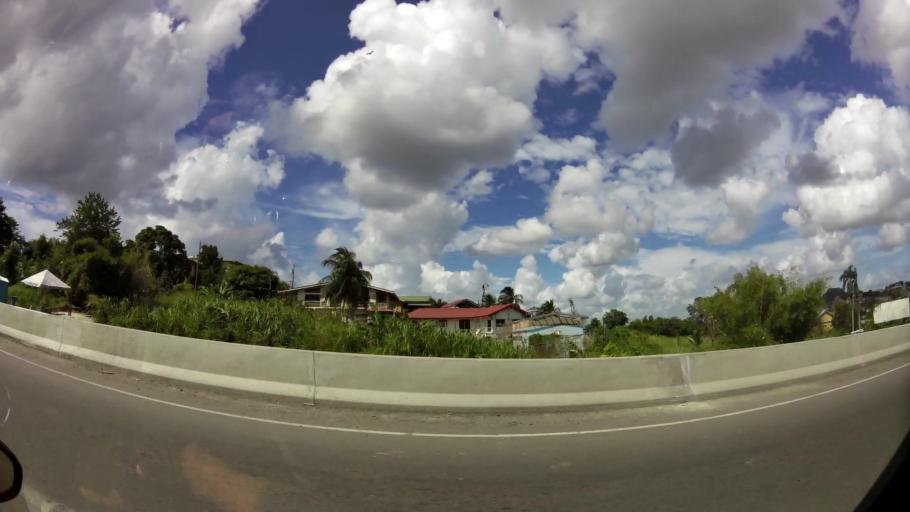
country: TT
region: City of San Fernando
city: San Fernando
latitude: 10.2558
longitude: -61.4779
